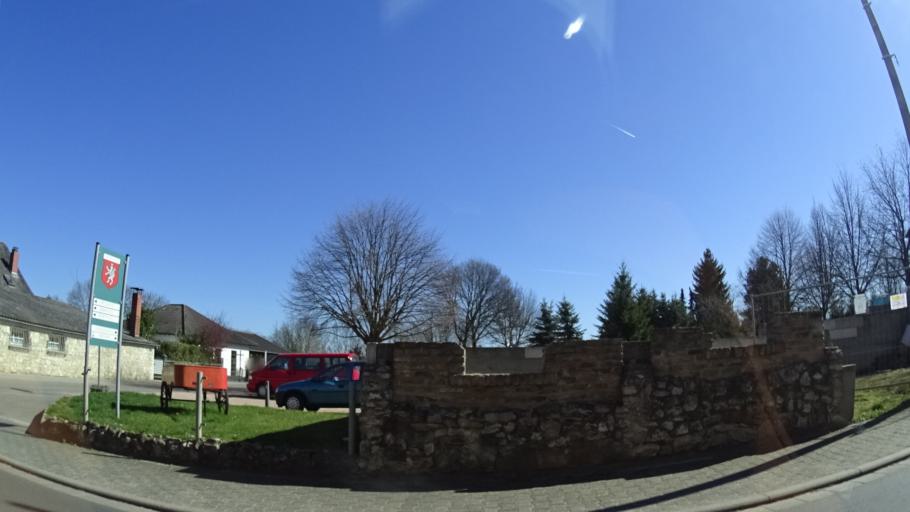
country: DE
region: Rheinland-Pfalz
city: Friesenheim
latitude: 49.8360
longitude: 8.2576
